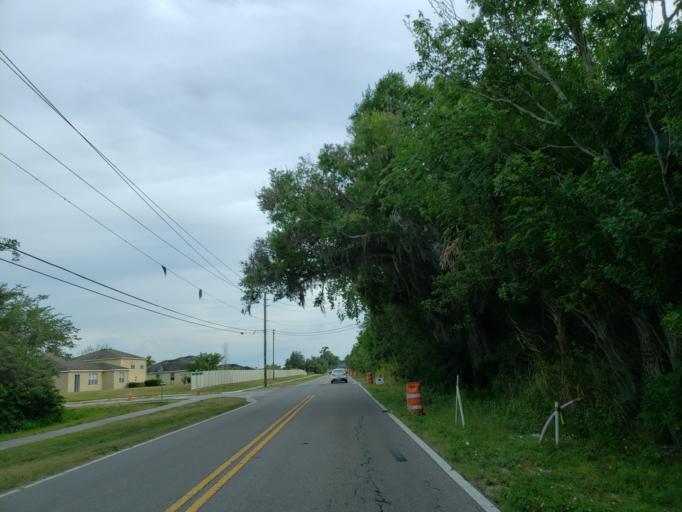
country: US
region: Florida
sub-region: Hillsborough County
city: Ruskin
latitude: 27.7417
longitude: -82.4187
